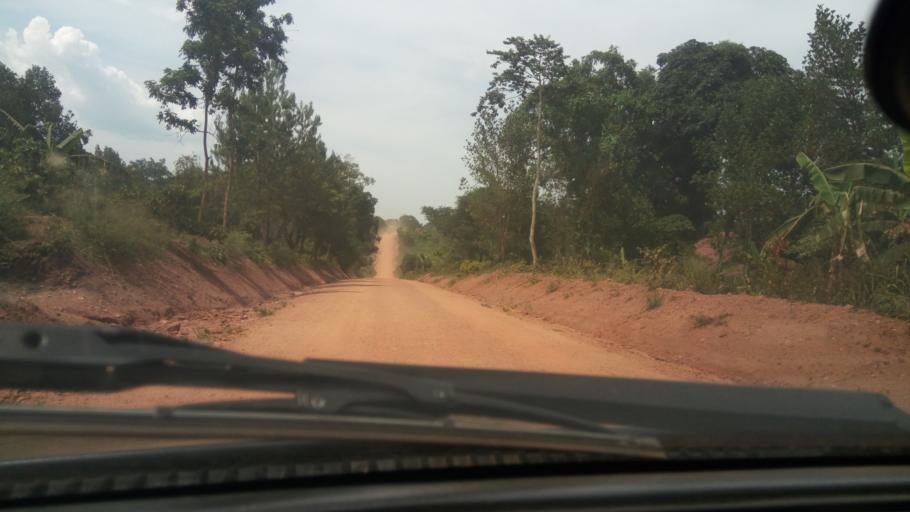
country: UG
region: Central Region
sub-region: Mityana District
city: Mityana
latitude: 0.4750
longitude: 32.1035
